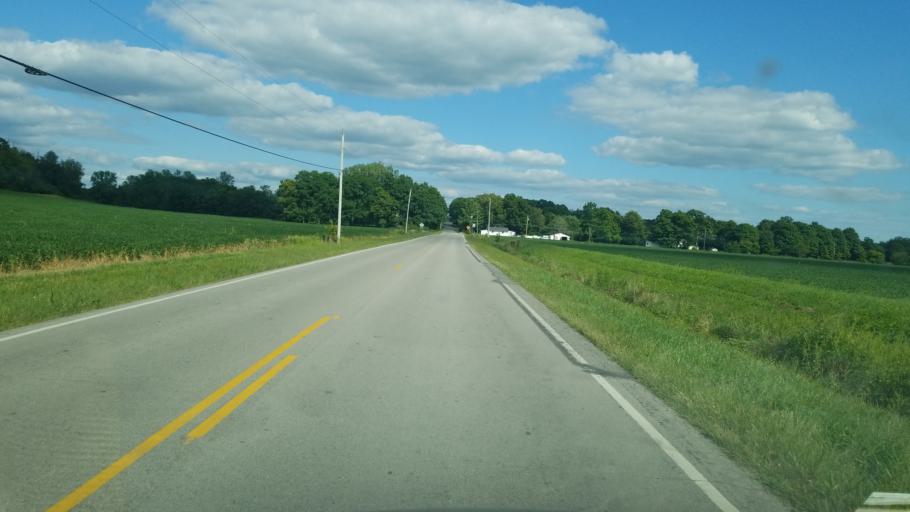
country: US
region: Ohio
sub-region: Champaign County
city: Saint Paris
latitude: 40.1583
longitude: -83.9266
